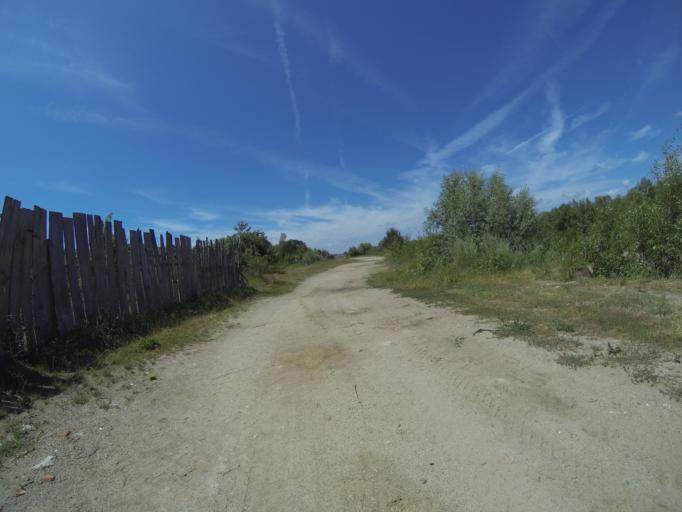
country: RO
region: Brasov
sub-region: Comuna Sinca Veche
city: Sinca Veche
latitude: 45.7546
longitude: 25.1794
